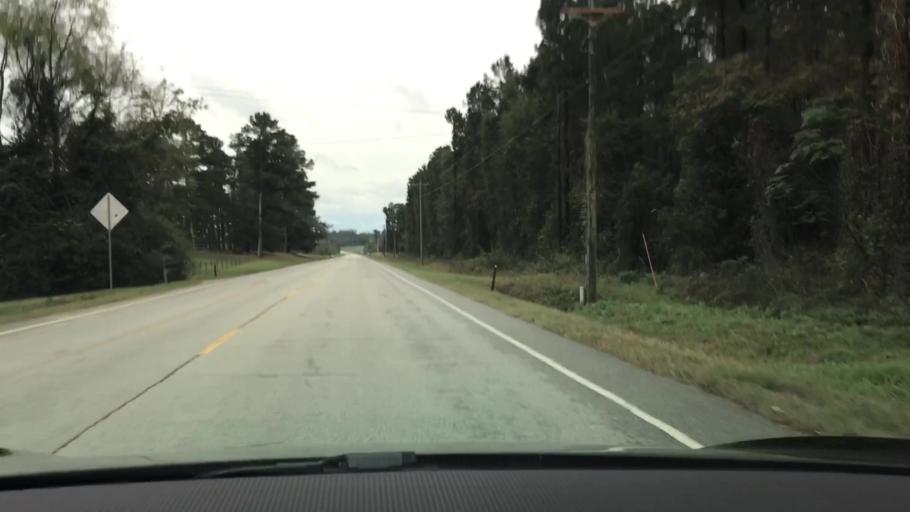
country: US
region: Georgia
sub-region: Jefferson County
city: Wrens
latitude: 33.1384
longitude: -82.4555
